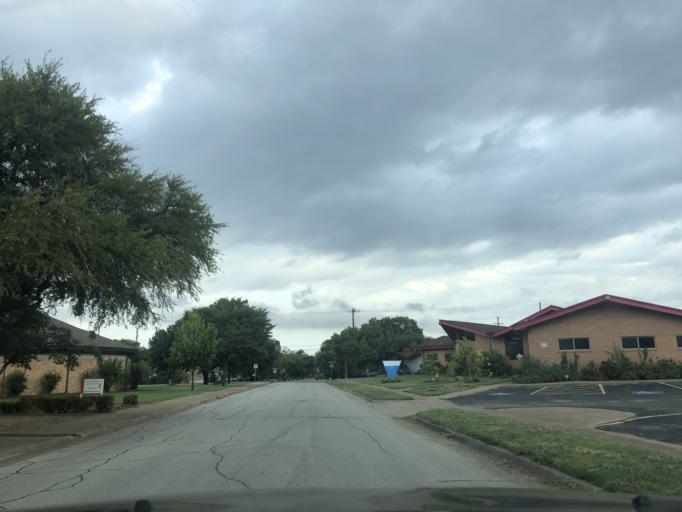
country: US
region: Texas
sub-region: Dallas County
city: Garland
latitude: 32.8776
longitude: -96.6524
